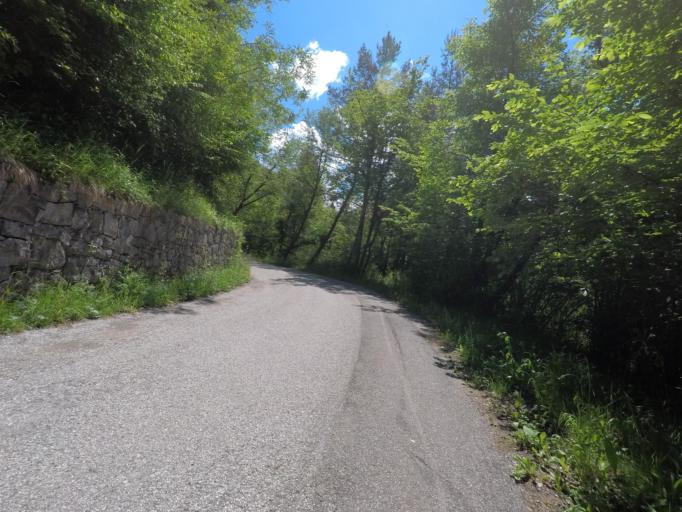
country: IT
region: Friuli Venezia Giulia
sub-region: Provincia di Udine
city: Raveo
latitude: 46.4414
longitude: 12.8827
